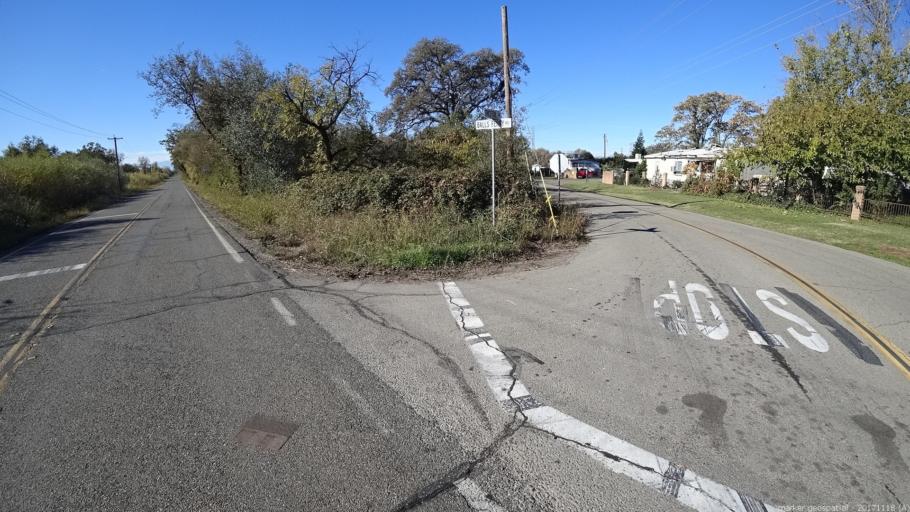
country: US
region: California
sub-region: Shasta County
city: Cottonwood
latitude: 40.3965
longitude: -122.2551
